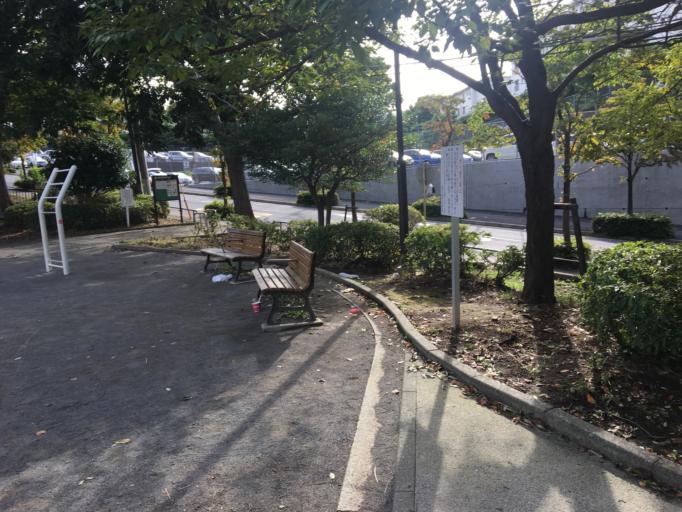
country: JP
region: Tokyo
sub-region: Machida-shi
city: Machida
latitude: 35.5447
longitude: 139.5177
